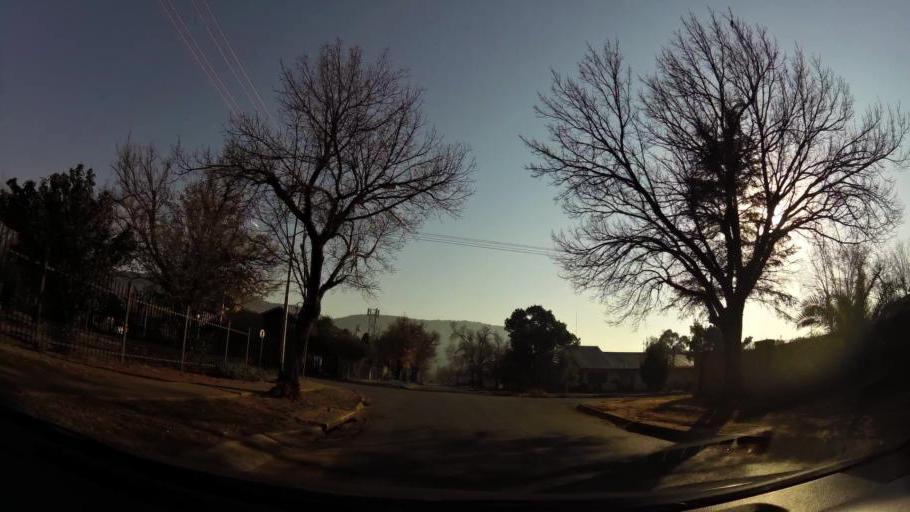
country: ZA
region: Gauteng
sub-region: City of Tshwane Metropolitan Municipality
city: Pretoria
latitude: -25.7054
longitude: 28.1768
